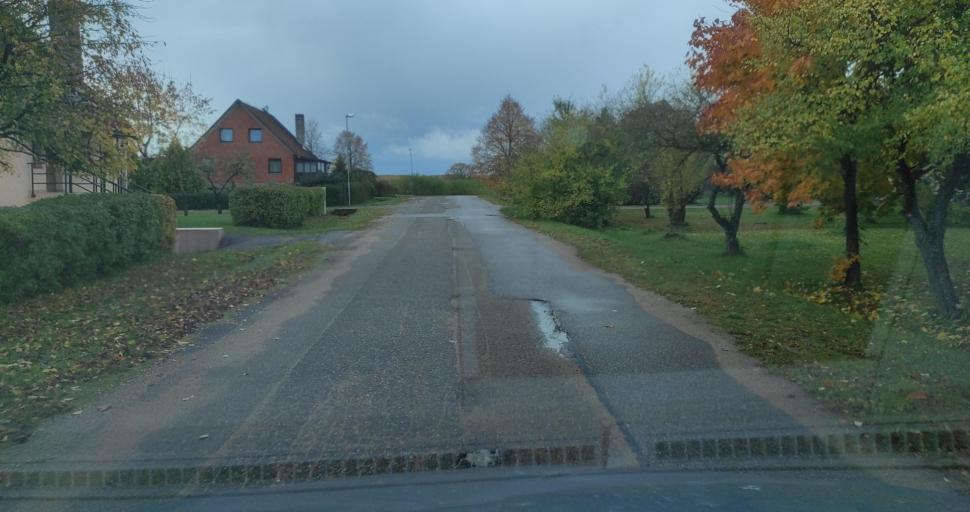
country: LV
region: Vainode
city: Vainode
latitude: 56.5729
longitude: 21.8963
